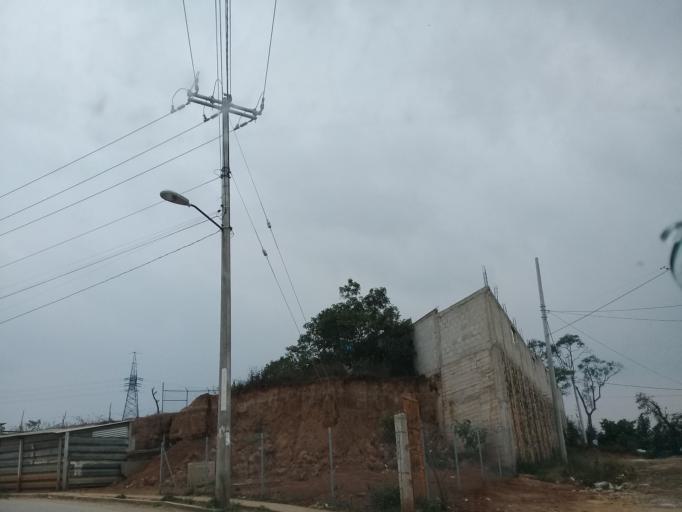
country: MX
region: Veracruz
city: El Castillo
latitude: 19.5624
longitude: -96.8866
